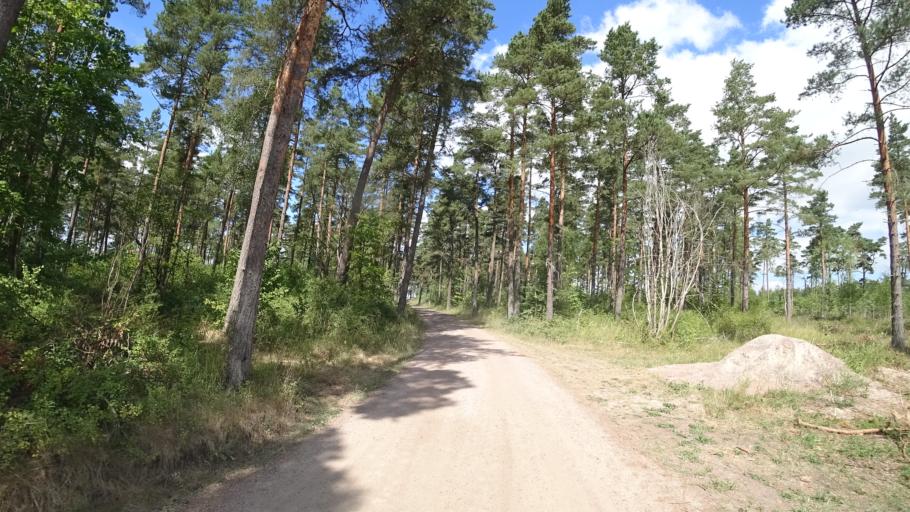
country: SE
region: Skane
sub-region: Kristianstads Kommun
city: Ahus
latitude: 55.9638
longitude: 14.2853
